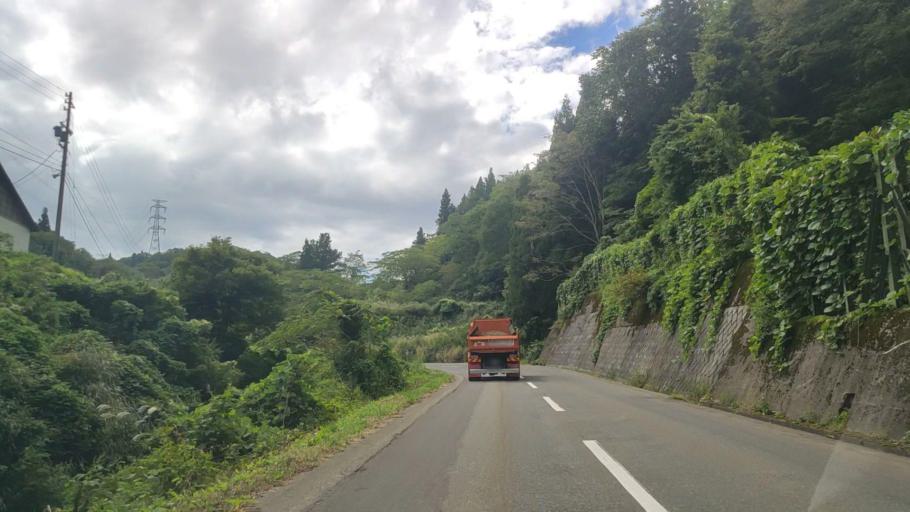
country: JP
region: Nagano
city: Iiyama
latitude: 36.8890
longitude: 138.3230
